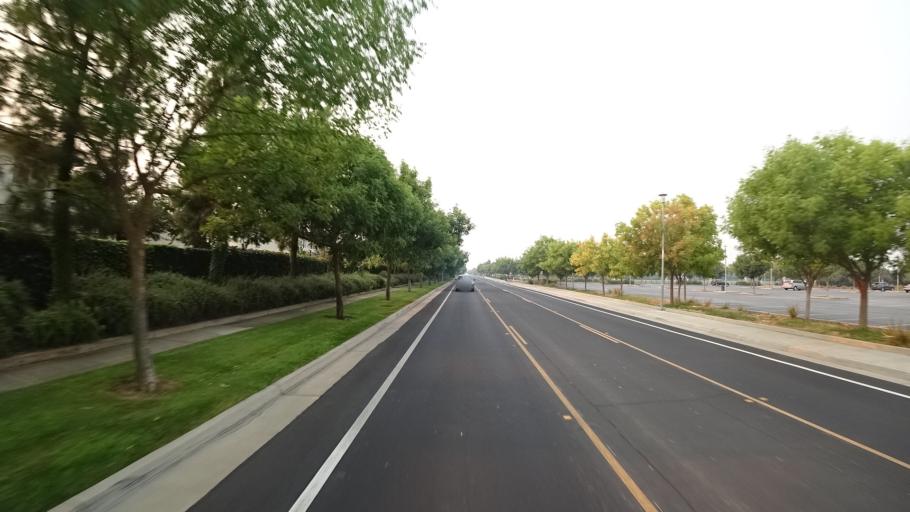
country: US
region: California
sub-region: Sacramento County
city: Laguna
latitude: 38.3921
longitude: -121.4222
